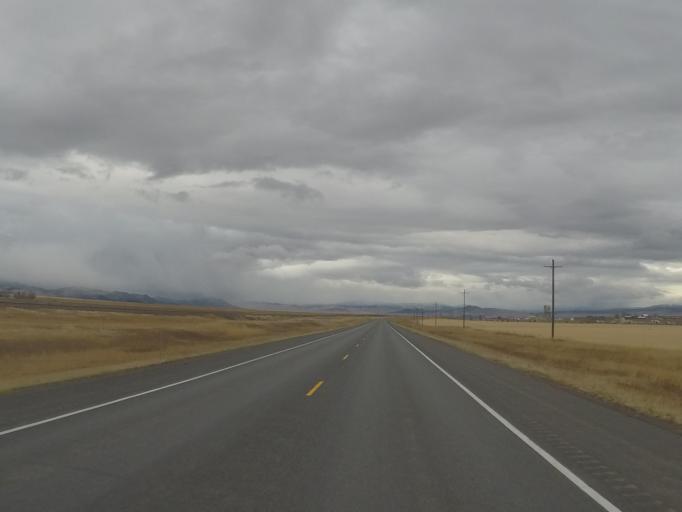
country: US
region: Montana
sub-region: Lewis and Clark County
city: East Helena
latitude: 46.5699
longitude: -111.8188
